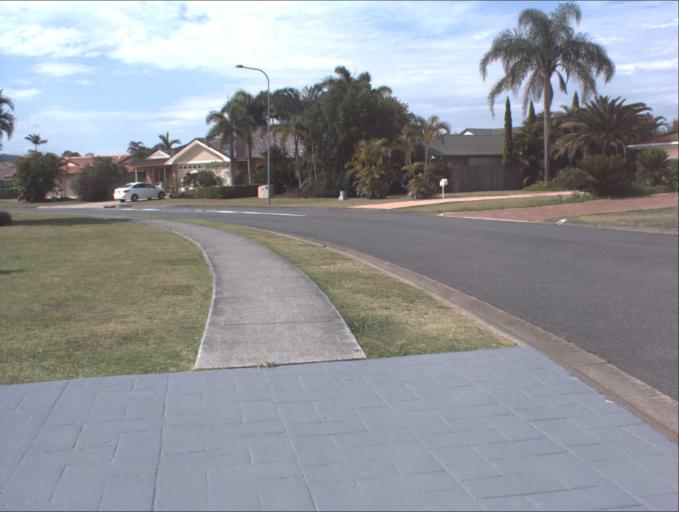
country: AU
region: Queensland
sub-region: Logan
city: Beenleigh
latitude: -27.6780
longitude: 153.2105
